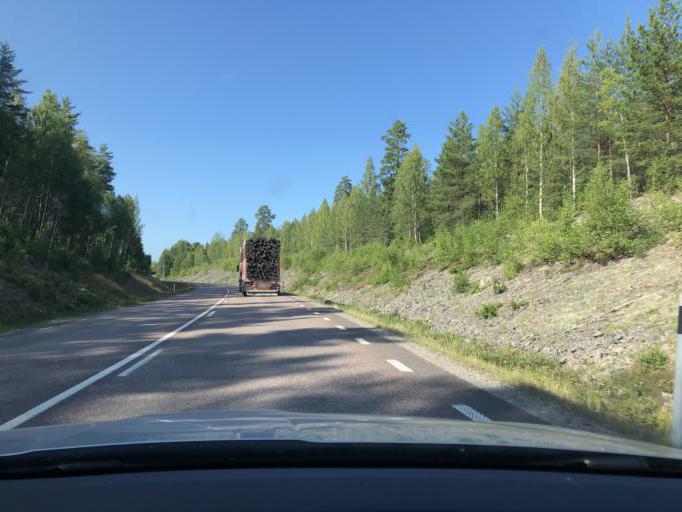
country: SE
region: Dalarna
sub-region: Faluns Kommun
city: Falun
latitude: 60.5821
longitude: 15.7740
